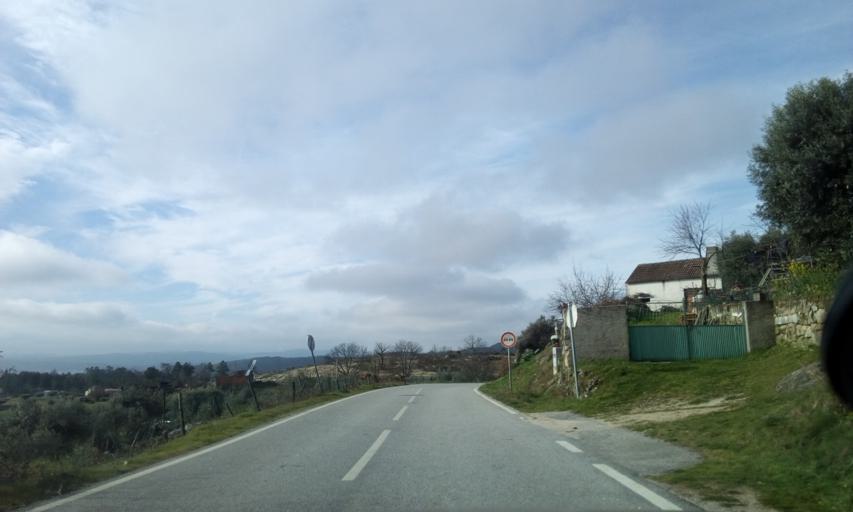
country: PT
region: Guarda
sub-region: Aguiar da Beira
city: Aguiar da Beira
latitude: 40.7470
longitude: -7.5538
